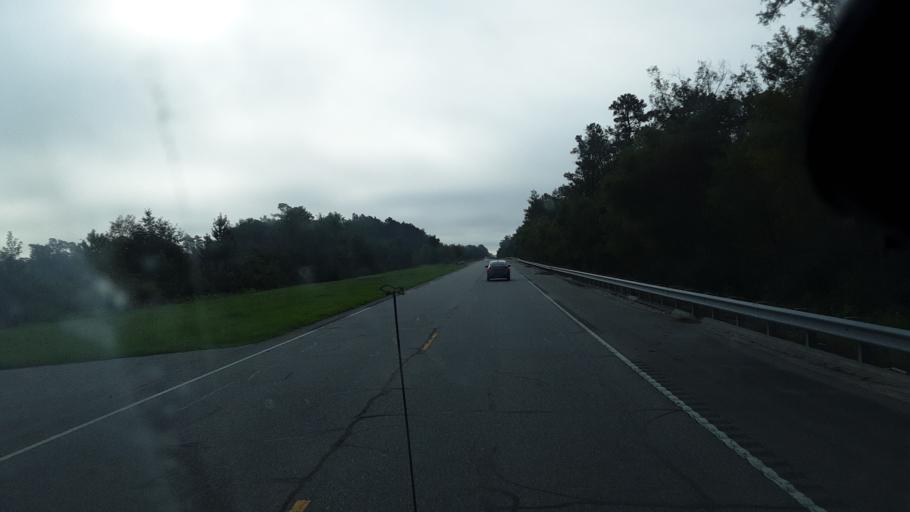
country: US
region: South Carolina
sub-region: Florence County
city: Johnsonville
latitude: 33.8586
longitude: -79.3161
